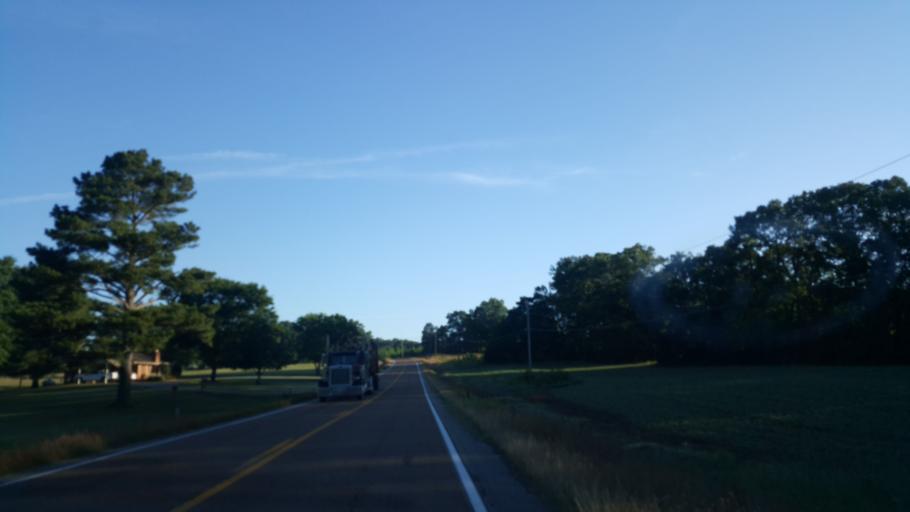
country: US
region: Tennessee
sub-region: McNairy County
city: Adamsville
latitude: 35.3296
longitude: -88.3560
